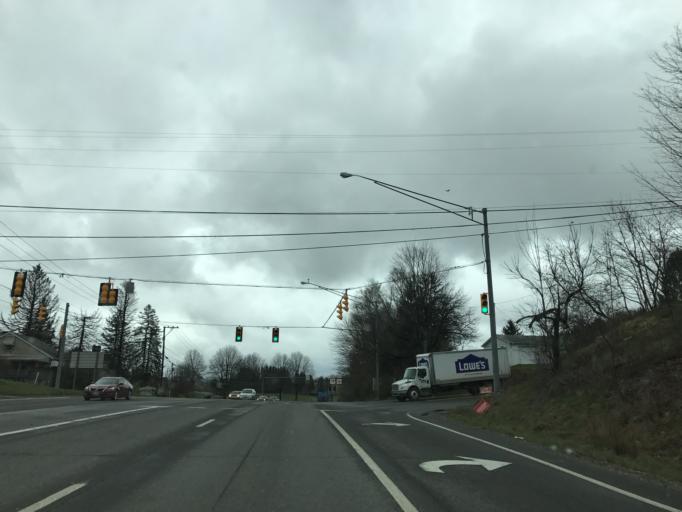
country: US
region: West Virginia
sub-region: Raleigh County
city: Prosperity
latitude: 37.8432
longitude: -81.1939
